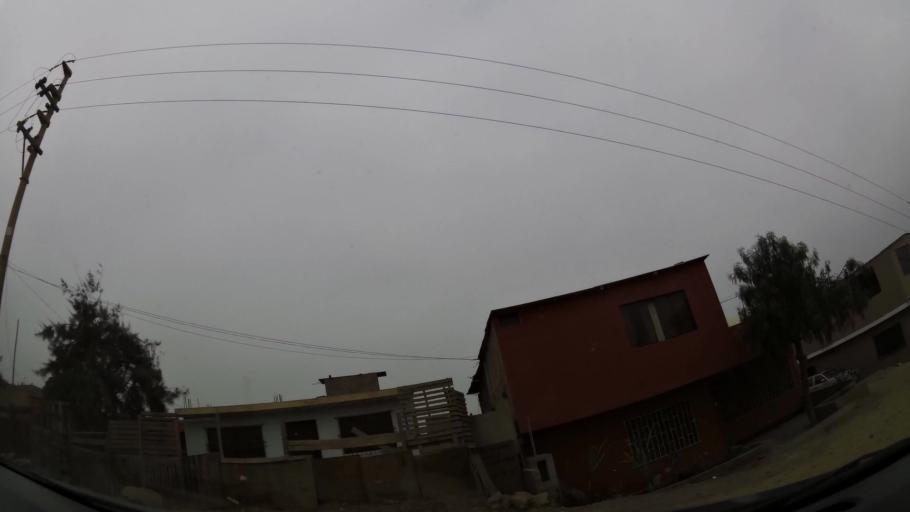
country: PE
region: Lima
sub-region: Lima
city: Surco
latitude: -12.2058
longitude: -76.9801
